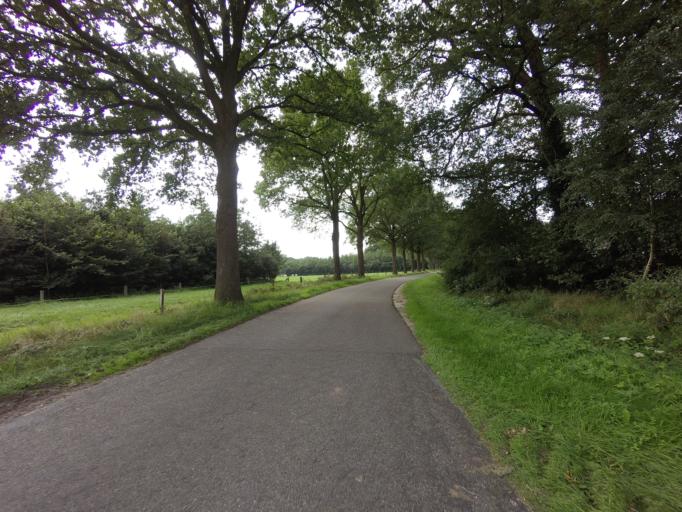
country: DE
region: Lower Saxony
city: Lage
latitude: 52.4303
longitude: 6.9339
